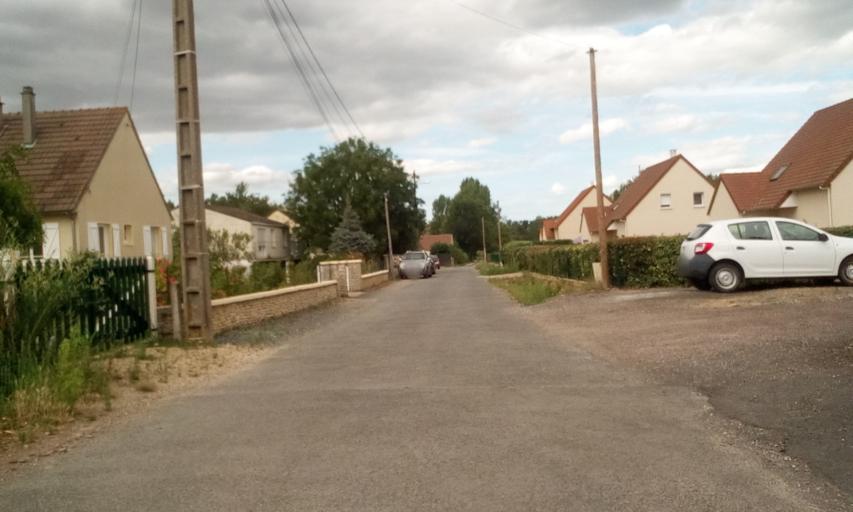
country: FR
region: Lower Normandy
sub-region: Departement du Calvados
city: Bellengreville
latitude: 49.1085
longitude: -0.2109
